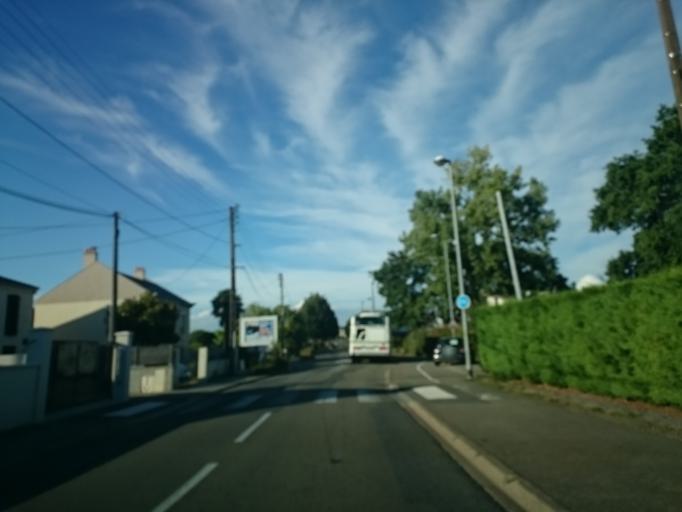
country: FR
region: Pays de la Loire
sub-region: Departement de la Loire-Atlantique
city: La Montagne
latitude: 47.1817
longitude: -1.6763
